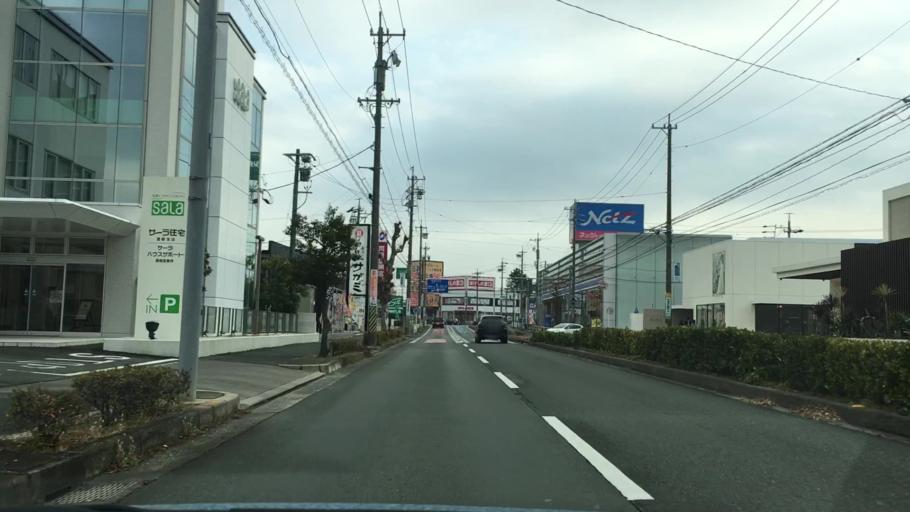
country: JP
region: Aichi
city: Toyohashi
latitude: 34.7507
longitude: 137.3755
